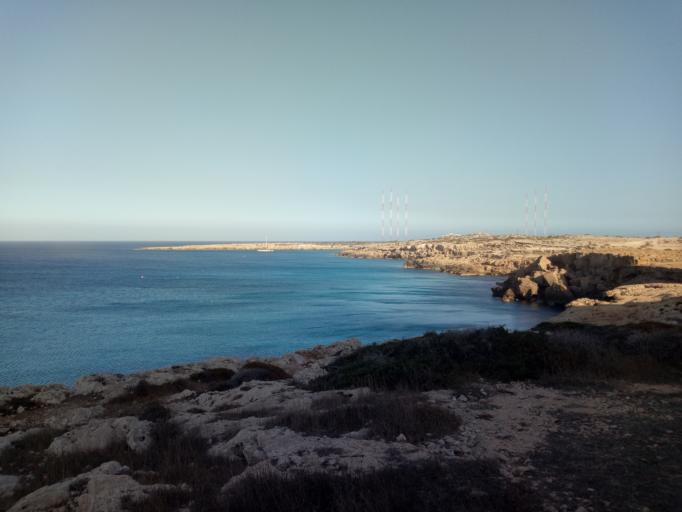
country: CY
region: Ammochostos
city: Protaras
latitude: 34.9694
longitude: 34.0758
